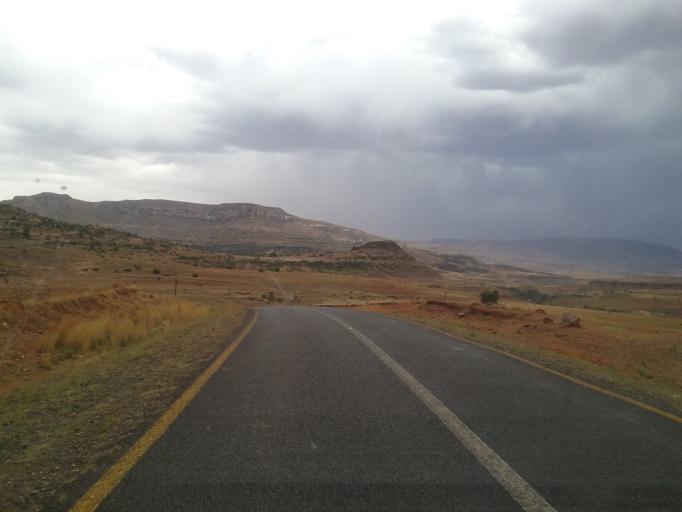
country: LS
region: Quthing
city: Quthing
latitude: -30.2932
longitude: 27.8126
